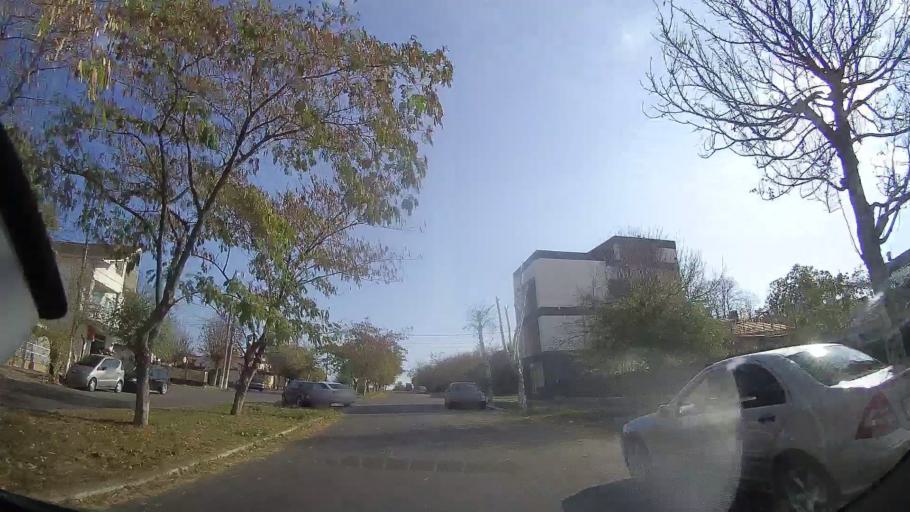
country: RO
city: Eforie Sud
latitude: 44.0208
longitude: 28.6482
